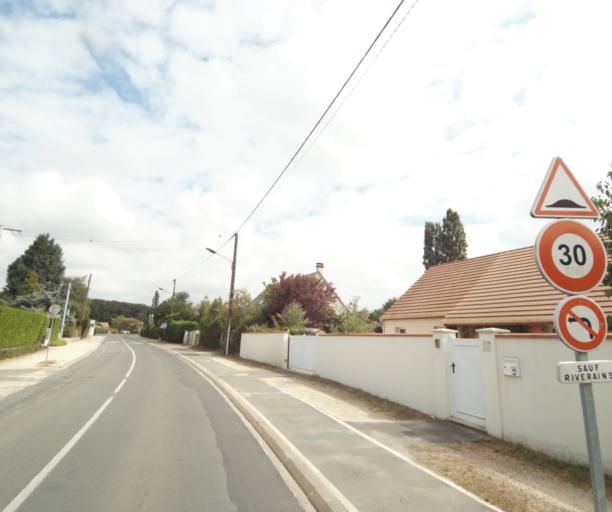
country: FR
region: Centre
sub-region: Departement du Loiret
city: Checy
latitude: 47.9013
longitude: 2.0279
